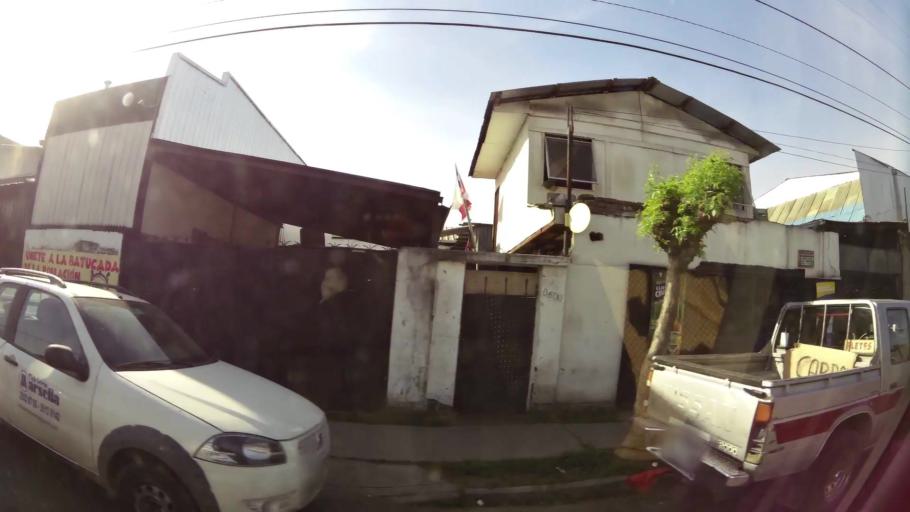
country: CL
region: Santiago Metropolitan
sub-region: Provincia de Santiago
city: La Pintana
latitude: -33.5232
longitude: -70.6281
